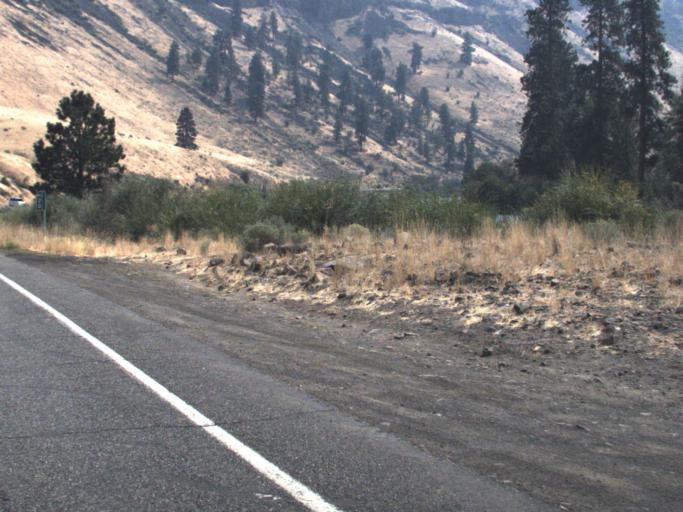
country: US
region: Washington
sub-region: Kittitas County
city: Kittitas
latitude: 46.8847
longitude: -120.4771
